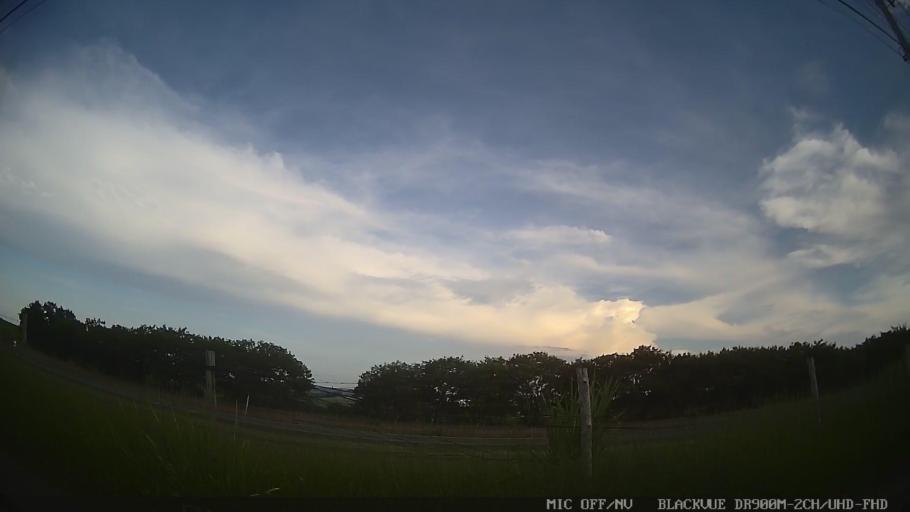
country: BR
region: Sao Paulo
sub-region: Tiete
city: Tiete
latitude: -23.0640
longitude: -47.7285
